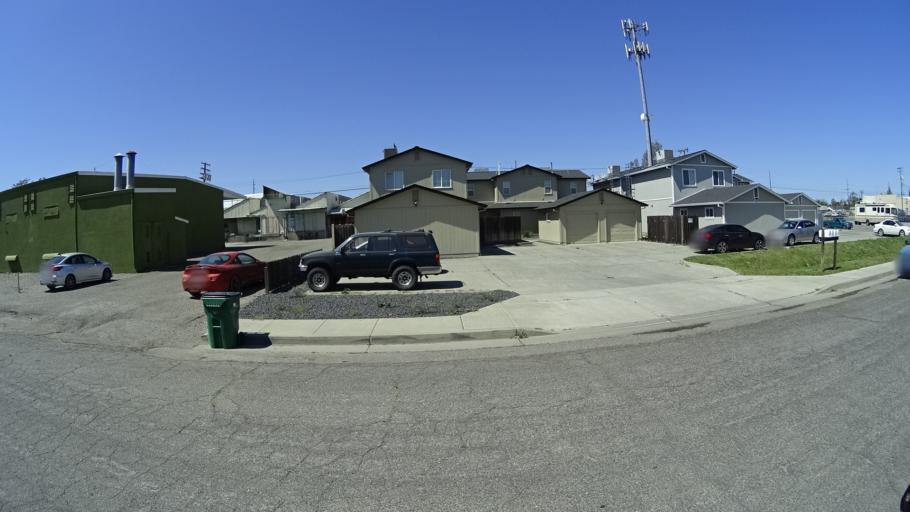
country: US
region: California
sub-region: Glenn County
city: Orland
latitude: 39.7505
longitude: -122.1954
